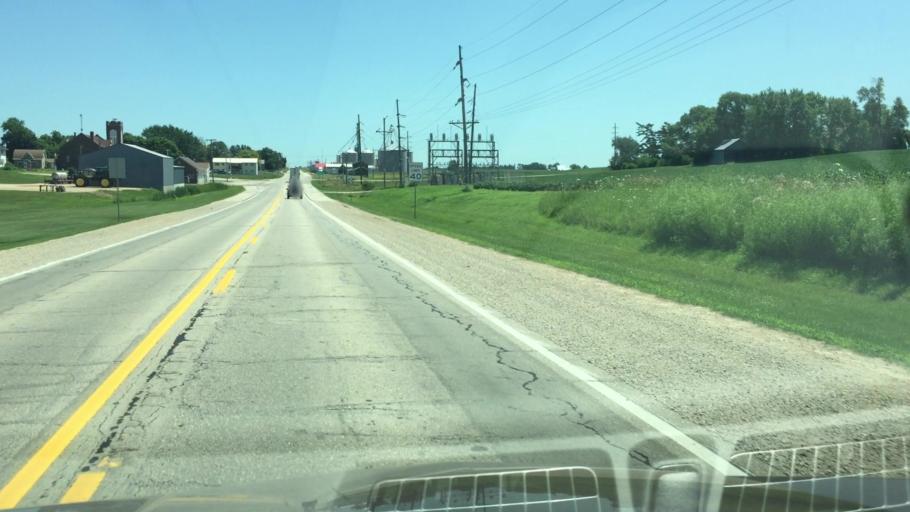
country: US
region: Iowa
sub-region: Cedar County
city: Mechanicsville
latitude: 41.8884
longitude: -91.1560
